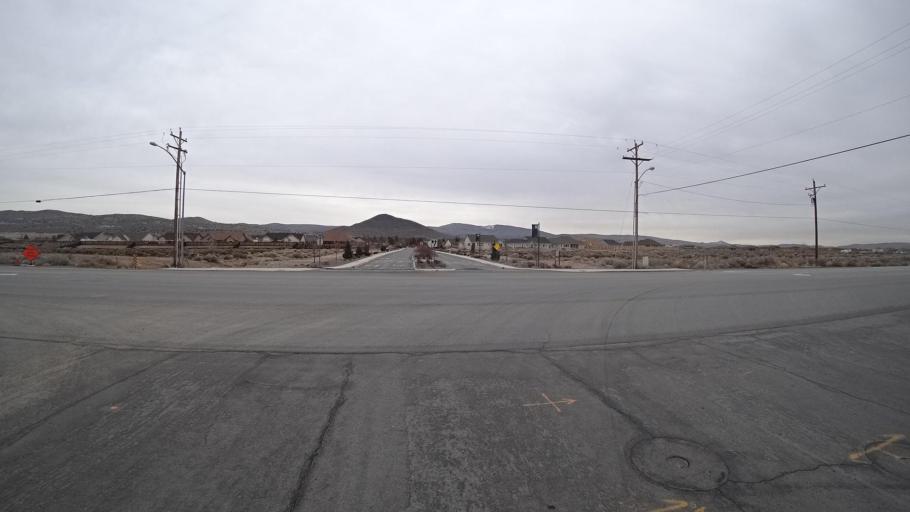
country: US
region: Nevada
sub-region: Washoe County
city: Spanish Springs
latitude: 39.6774
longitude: -119.7010
